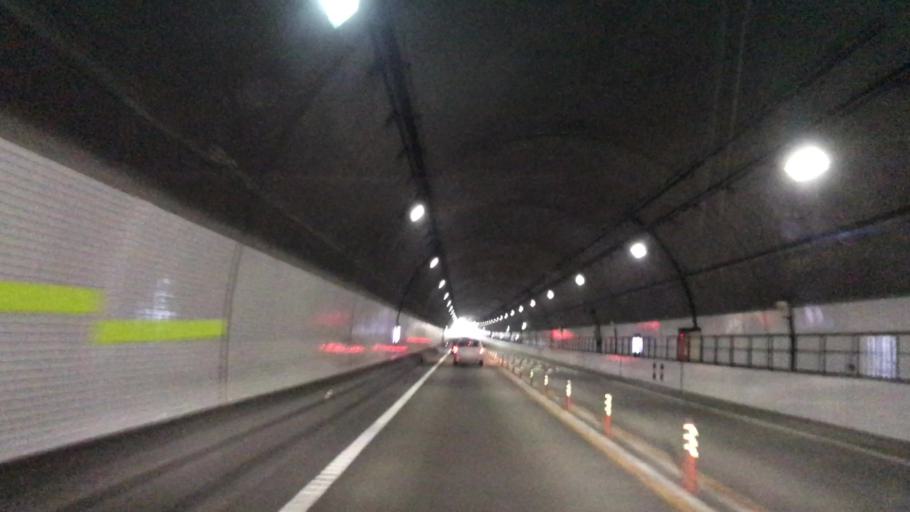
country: JP
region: Hokkaido
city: Shimo-furano
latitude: 42.9536
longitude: 142.3161
